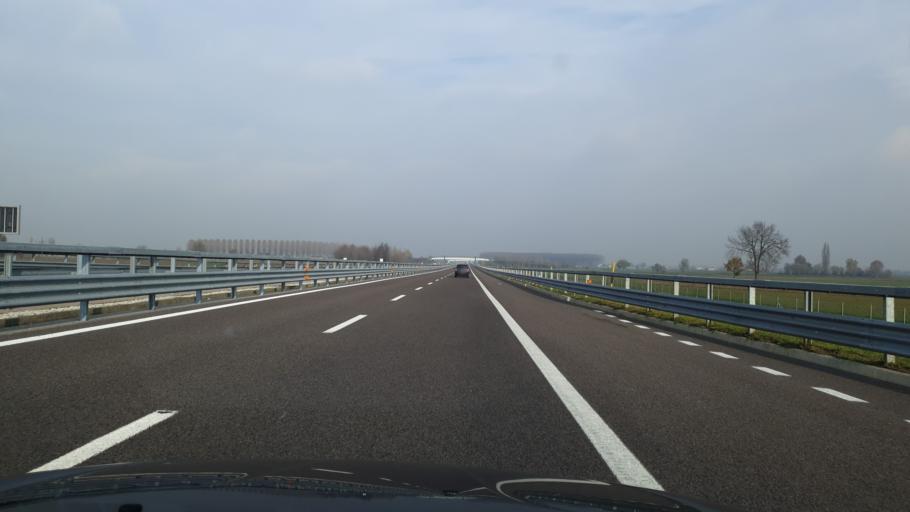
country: IT
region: Veneto
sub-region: Provincia di Padova
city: Megliadino San Vitale
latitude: 45.1780
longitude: 11.5362
